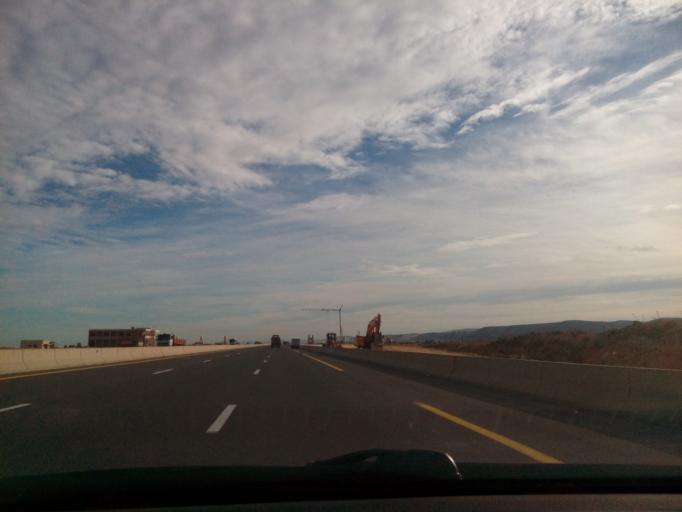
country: DZ
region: Mascara
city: Sig
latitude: 35.5419
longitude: -0.3582
